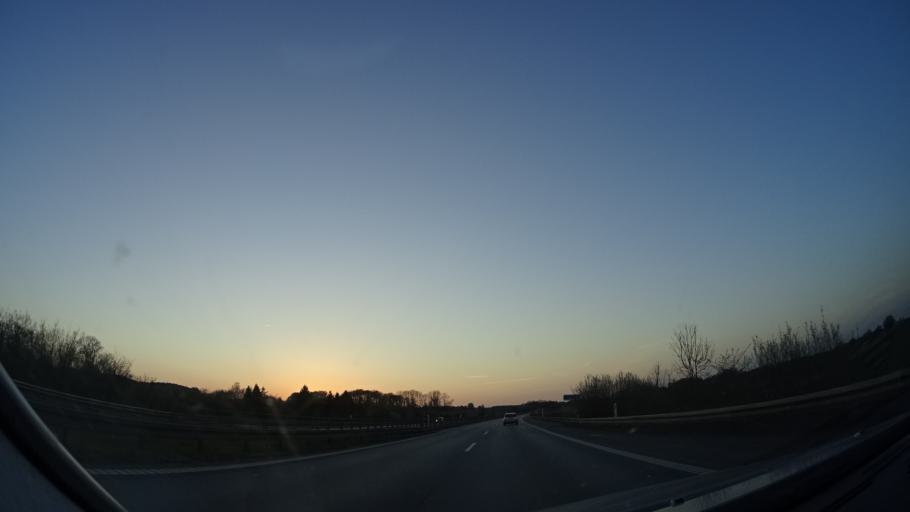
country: DK
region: Zealand
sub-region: Lejre Kommune
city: Lejre
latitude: 55.6271
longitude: 11.9698
